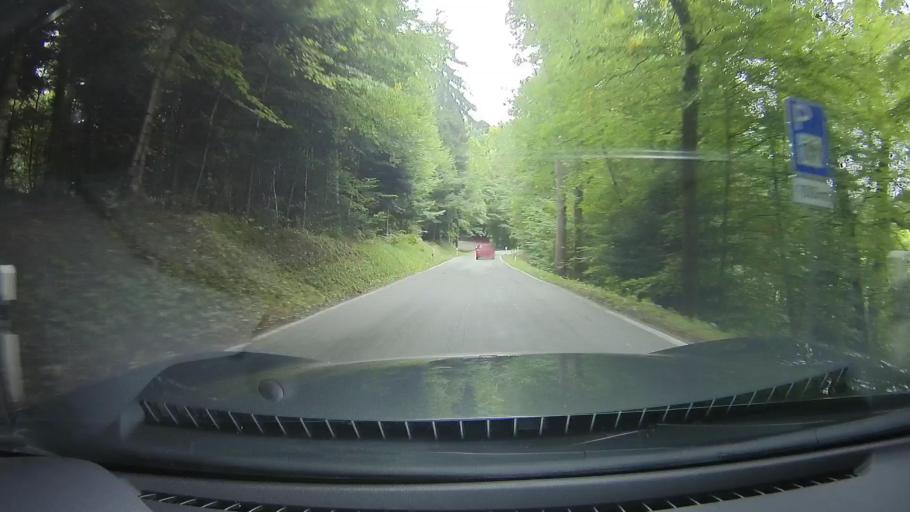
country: DE
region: Baden-Wuerttemberg
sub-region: Regierungsbezirk Stuttgart
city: Althutte
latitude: 48.9343
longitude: 9.5650
